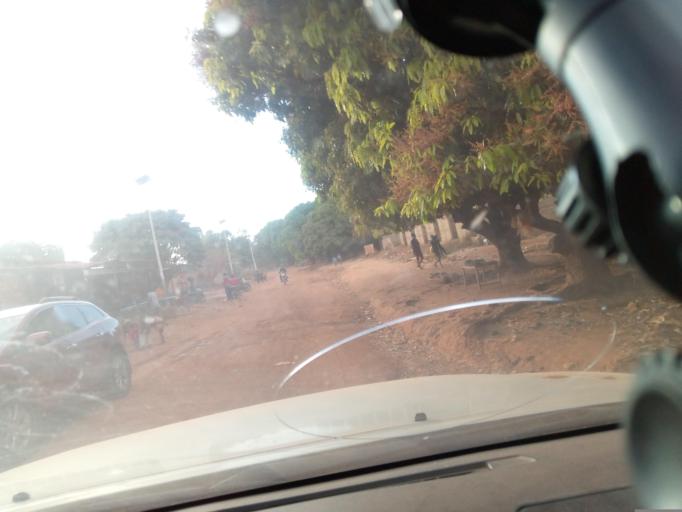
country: ML
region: Sikasso
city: Sikasso
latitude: 11.3164
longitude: -5.6396
